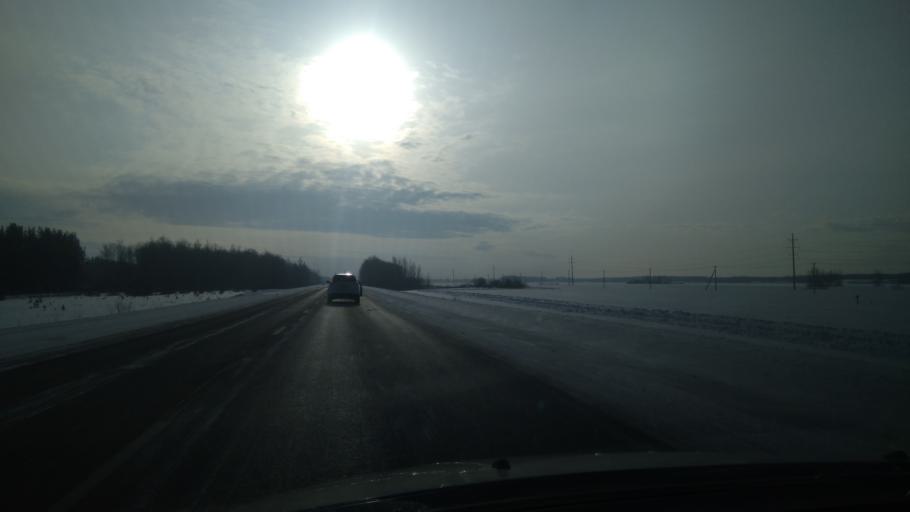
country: RU
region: Sverdlovsk
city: Sukhoy Log
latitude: 56.8627
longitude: 62.0476
